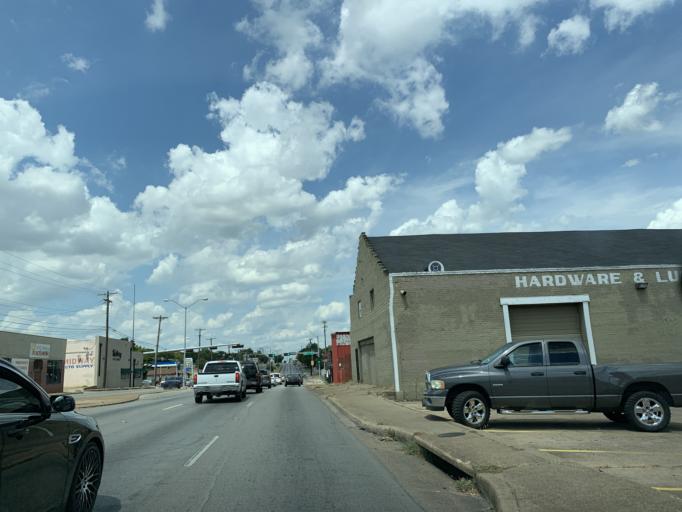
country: US
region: Texas
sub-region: Dallas County
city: Cockrell Hill
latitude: 32.7339
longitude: -96.8568
